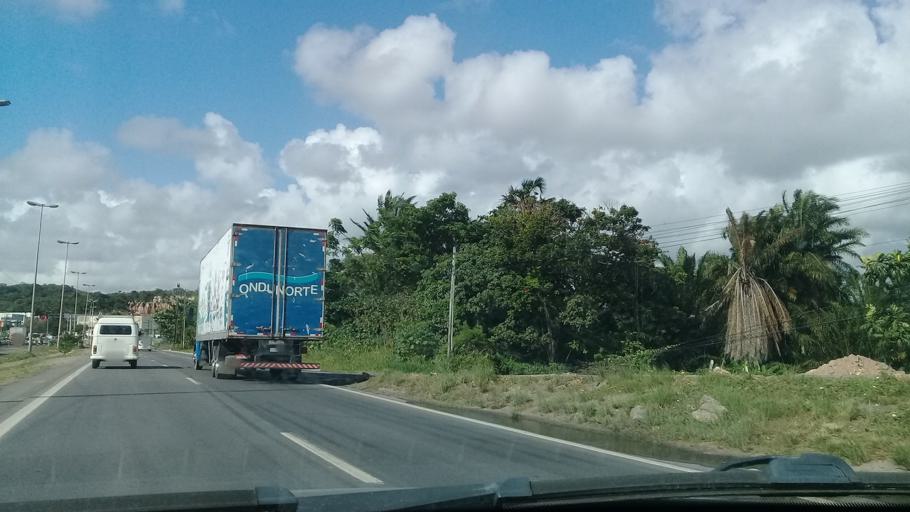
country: BR
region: Pernambuco
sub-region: Jaboatao Dos Guararapes
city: Jaboatao dos Guararapes
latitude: -8.0935
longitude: -34.9478
